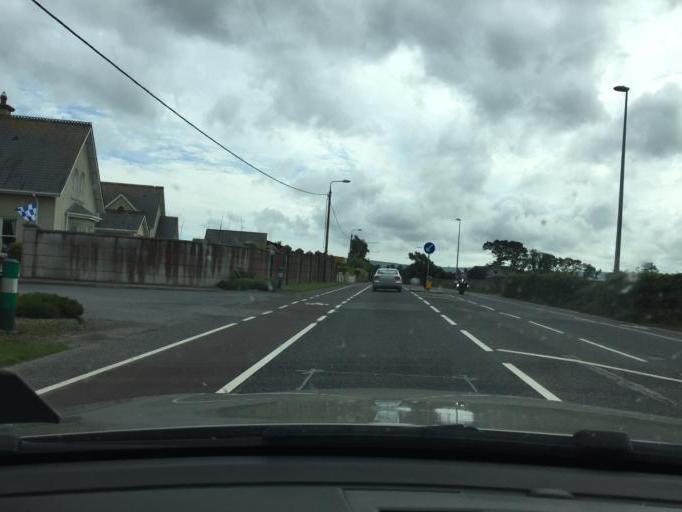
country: IE
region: Munster
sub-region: Waterford
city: Dungarvan
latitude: 52.1053
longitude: -7.6038
